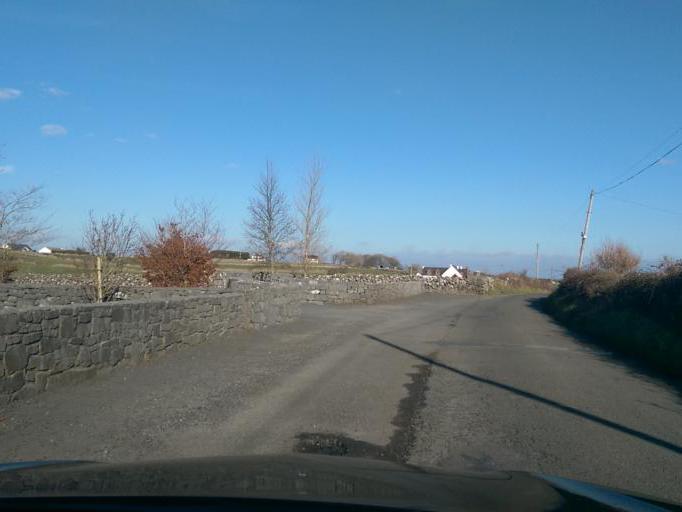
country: IE
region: Connaught
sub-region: County Galway
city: Oranmore
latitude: 53.2234
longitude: -8.9393
